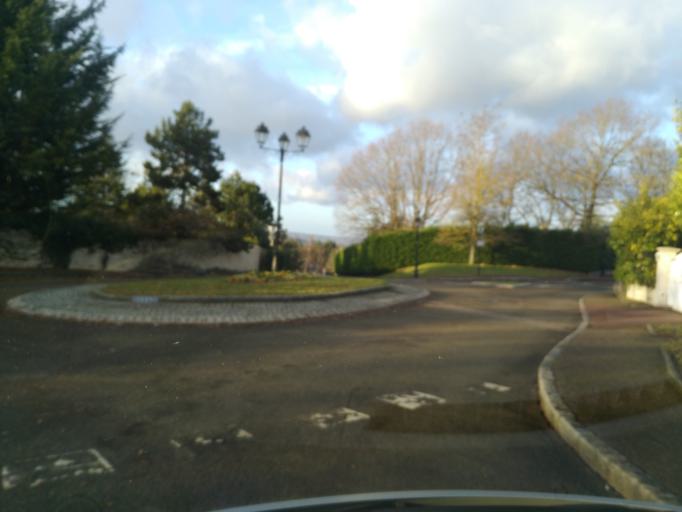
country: FR
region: Ile-de-France
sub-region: Departement des Yvelines
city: Chambourcy
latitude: 48.9007
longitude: 2.0326
